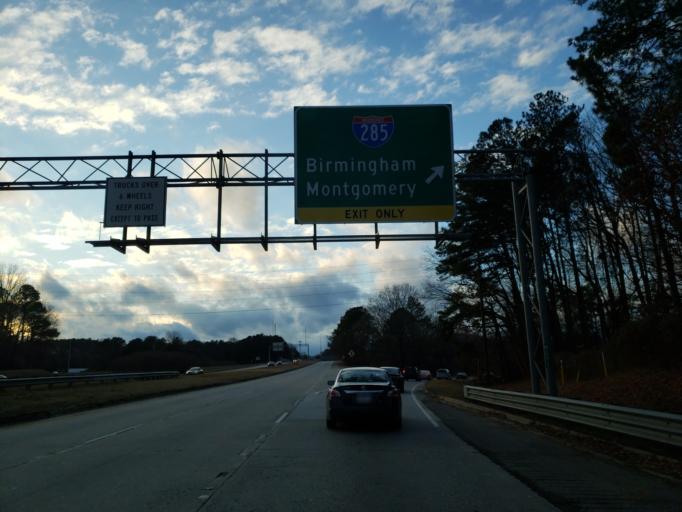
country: US
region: Georgia
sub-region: Fulton County
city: East Point
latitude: 33.6903
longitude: -84.4962
